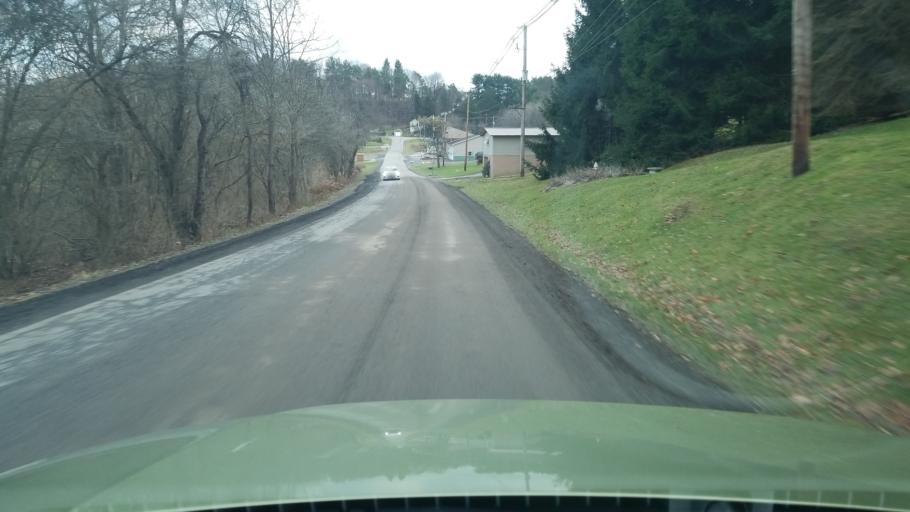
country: US
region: Pennsylvania
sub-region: Clearfield County
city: DuBois
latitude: 41.1293
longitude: -78.7797
